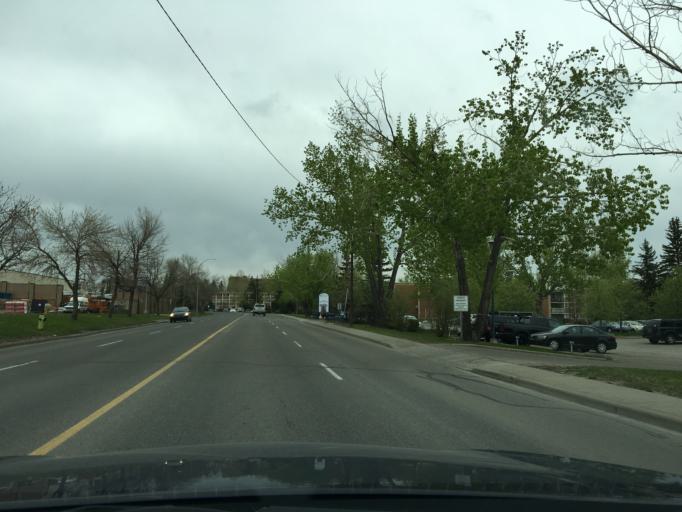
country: CA
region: Alberta
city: Calgary
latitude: 50.9660
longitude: -114.0681
